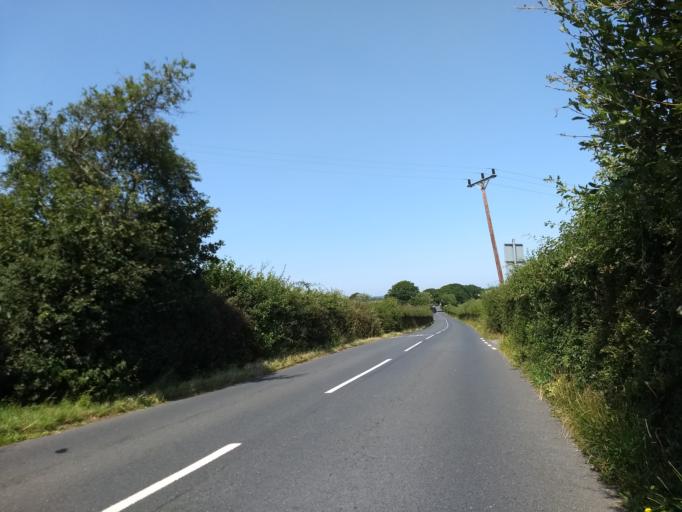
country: GB
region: England
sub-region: Isle of Wight
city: Northwood
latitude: 50.7230
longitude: -1.3534
